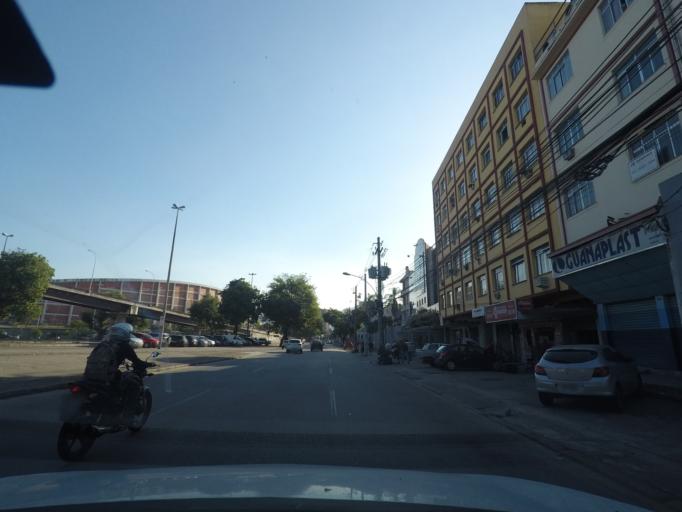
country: BR
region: Rio de Janeiro
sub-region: Rio De Janeiro
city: Rio de Janeiro
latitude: -22.8949
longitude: -43.2202
